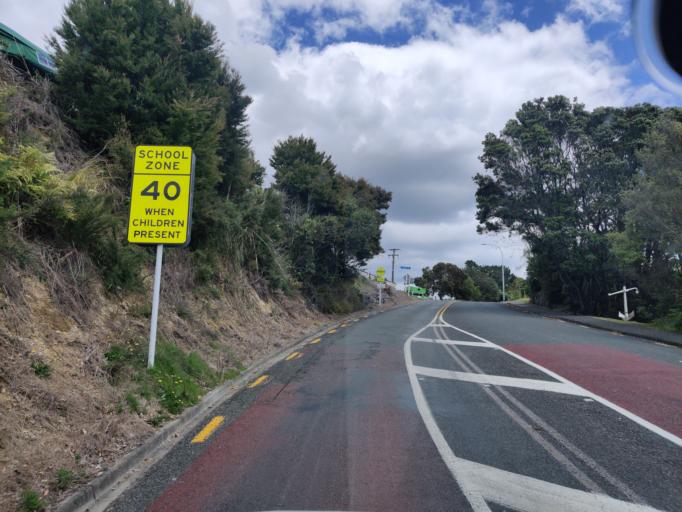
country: NZ
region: Northland
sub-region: Far North District
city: Paihia
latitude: -35.3140
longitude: 174.1189
